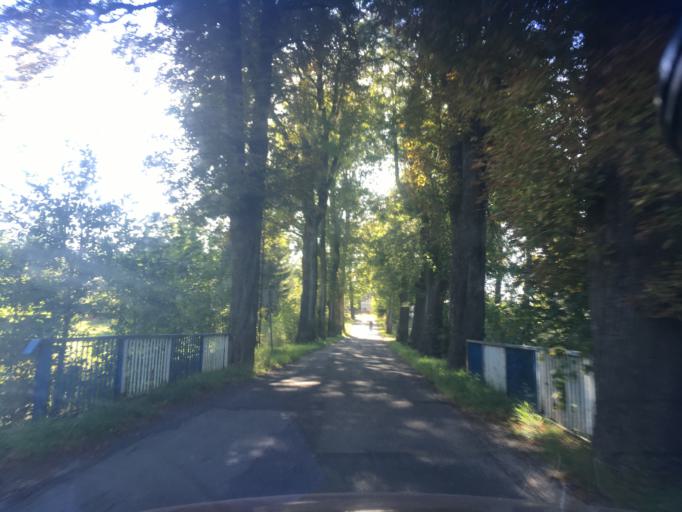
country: PL
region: Lower Silesian Voivodeship
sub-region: Powiat lubanski
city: Swieradow-Zdroj
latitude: 50.9310
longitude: 15.2890
